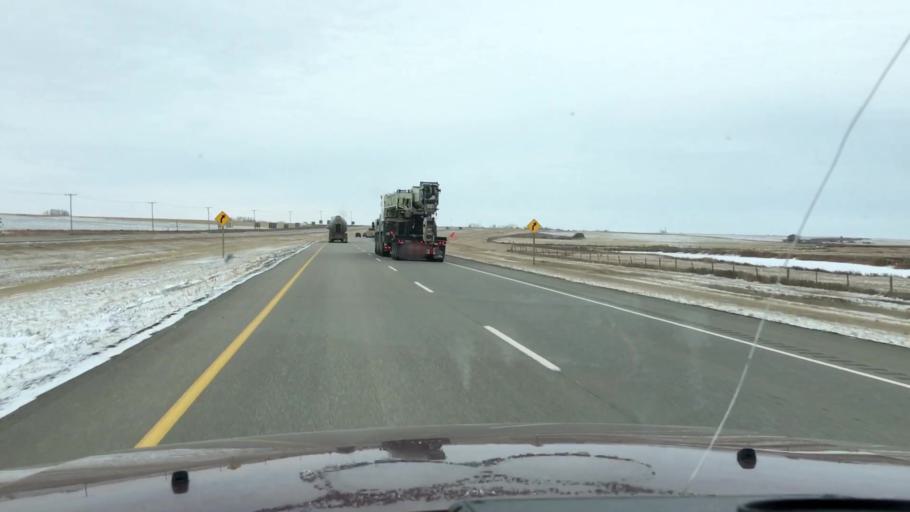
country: CA
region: Saskatchewan
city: Watrous
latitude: 51.2385
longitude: -105.9641
